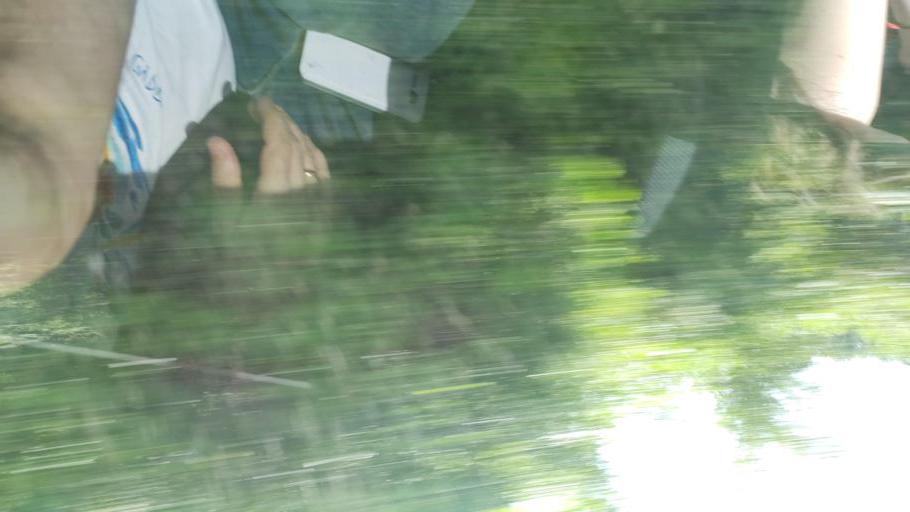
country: RO
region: Mehedinti
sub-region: Comuna Eselnita
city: Eselnita
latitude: 44.7136
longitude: 22.3589
